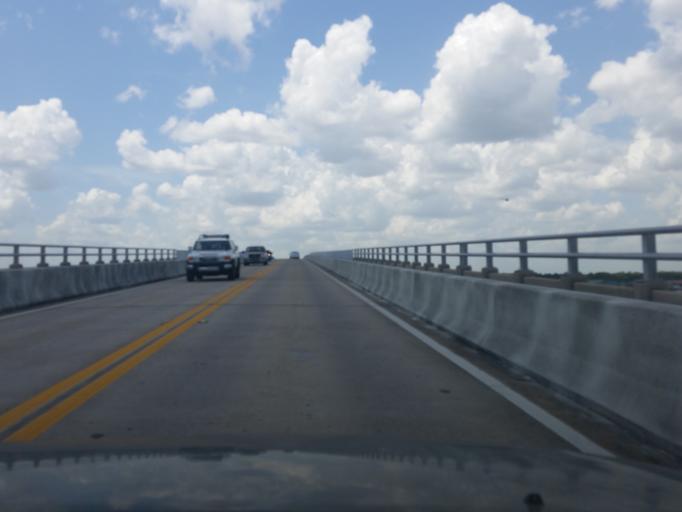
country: US
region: Florida
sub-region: Santa Rosa County
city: Navarre
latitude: 30.3948
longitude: -86.8631
